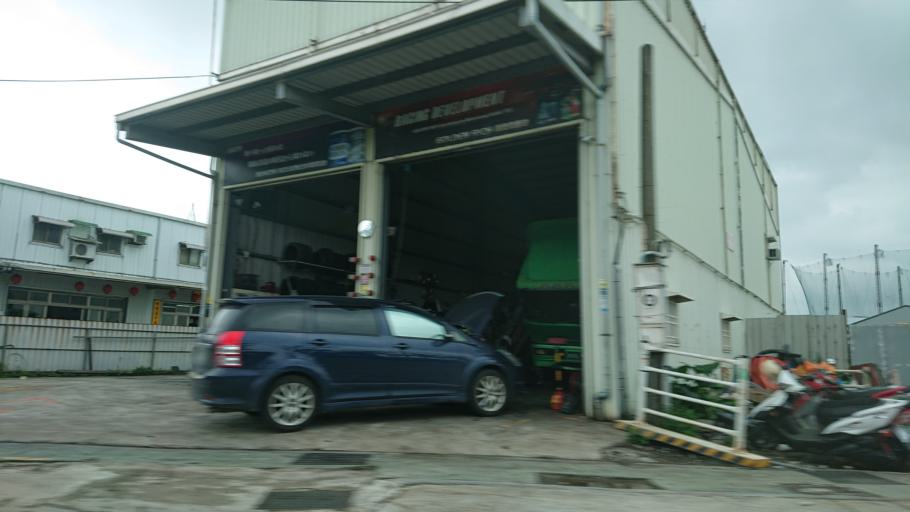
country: TW
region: Taiwan
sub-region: Taoyuan
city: Taoyuan
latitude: 24.9614
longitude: 121.3160
